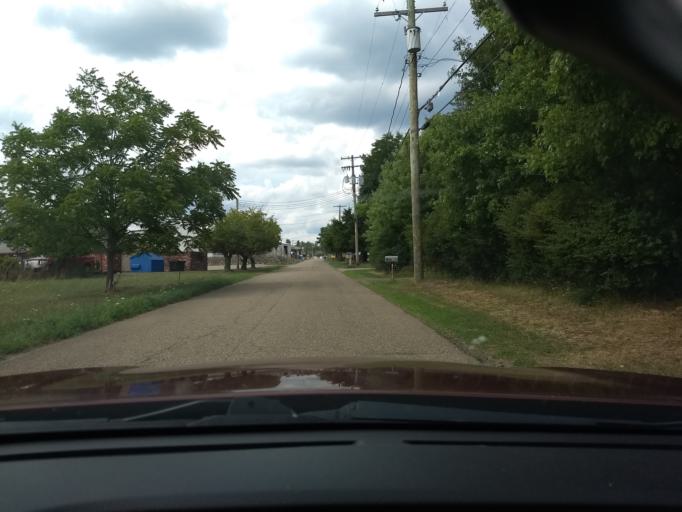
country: US
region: Pennsylvania
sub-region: Armstrong County
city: Freeport
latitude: 40.6415
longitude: -79.7096
